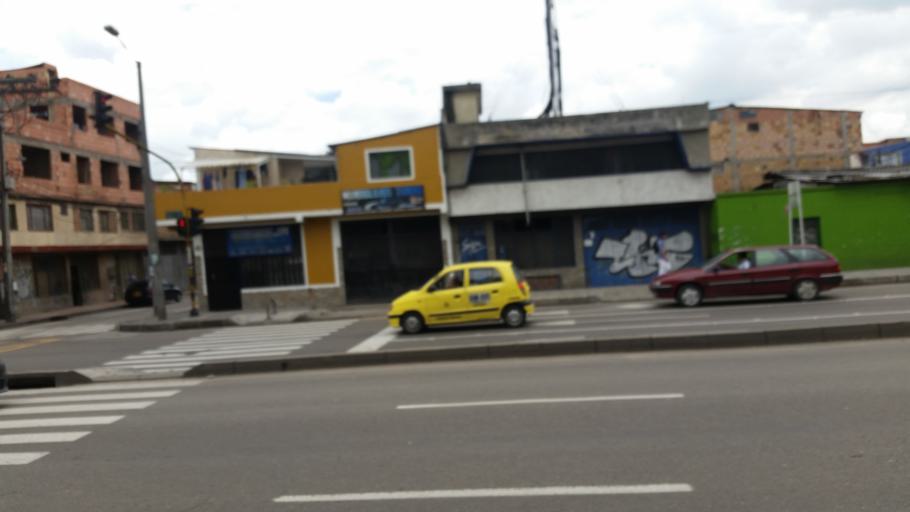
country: CO
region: Cundinamarca
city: Funza
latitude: 4.6997
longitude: -74.1311
